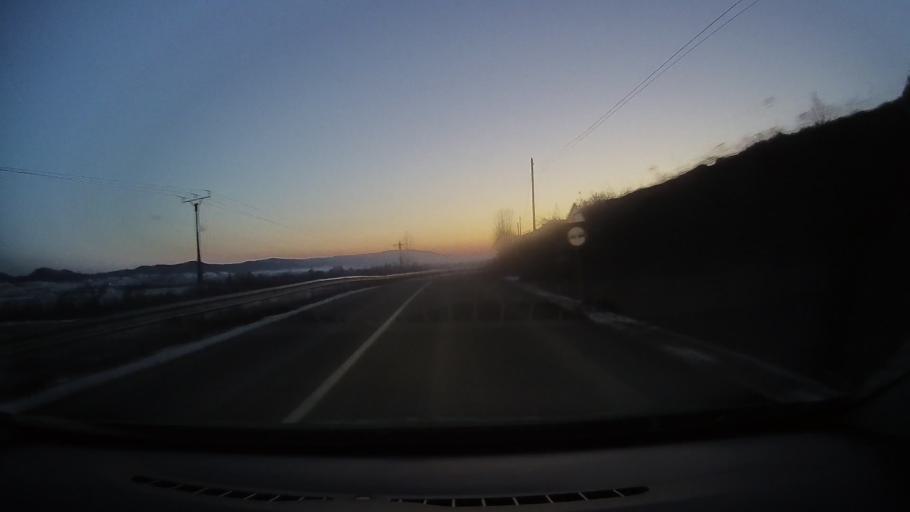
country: RO
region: Sibiu
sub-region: Comuna Brateiu
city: Brateiu
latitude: 46.1935
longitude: 24.4399
